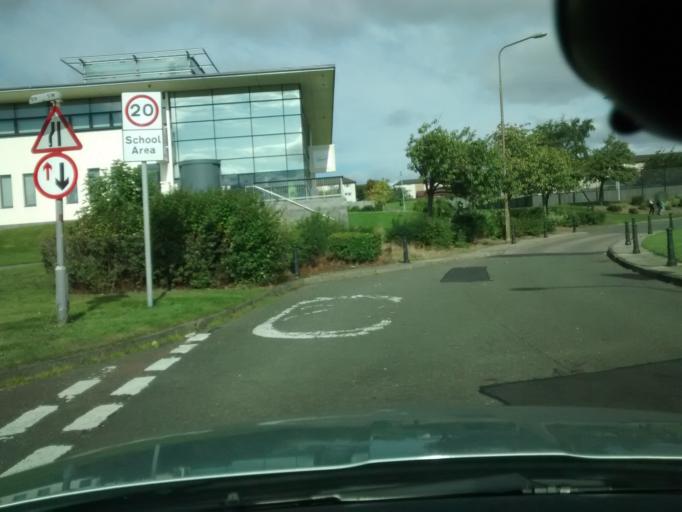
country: GB
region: Scotland
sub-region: West Lothian
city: Mid Calder
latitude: 55.8937
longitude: -3.5021
